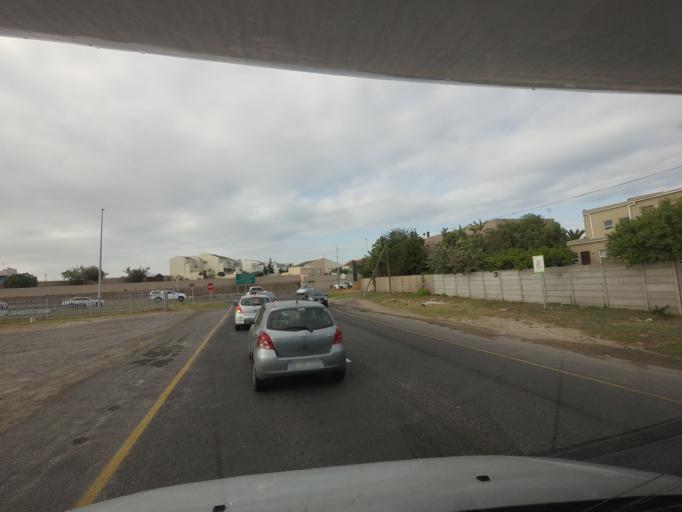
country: ZA
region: Western Cape
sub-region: City of Cape Town
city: Sunset Beach
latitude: -33.7265
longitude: 18.4475
